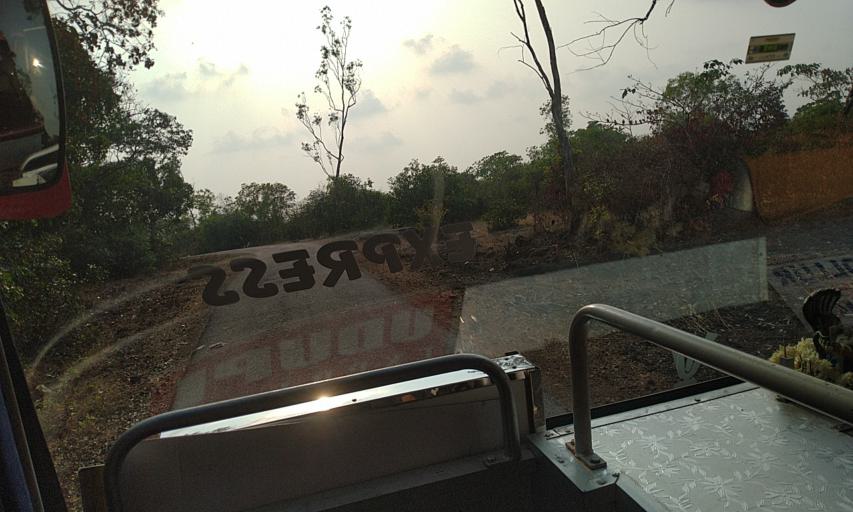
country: IN
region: Karnataka
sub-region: Udupi
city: Byndoor
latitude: 13.8125
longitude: 74.7079
